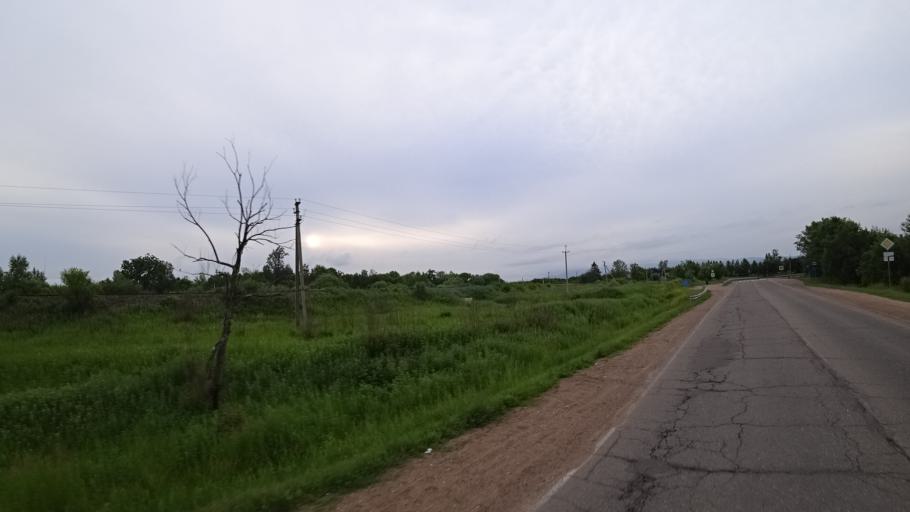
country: RU
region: Primorskiy
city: Novosysoyevka
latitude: 44.2255
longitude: 133.3509
